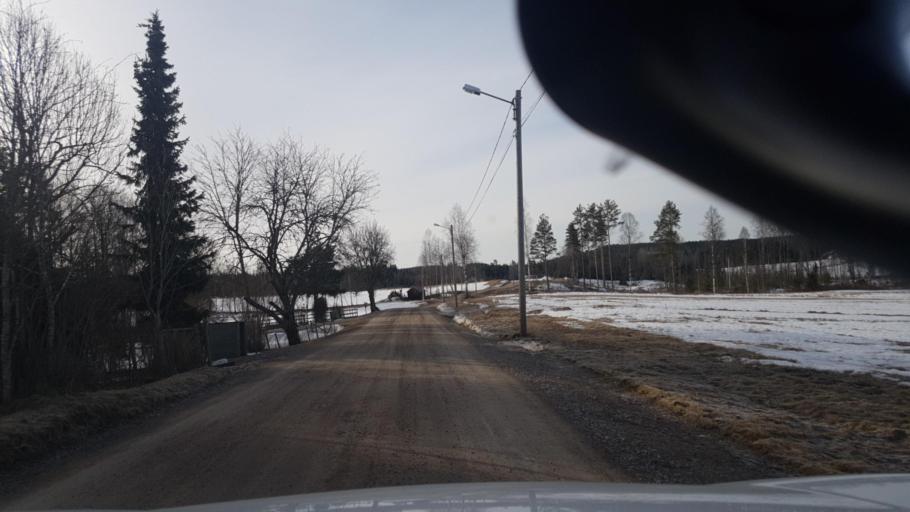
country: SE
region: Vaermland
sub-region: Arvika Kommun
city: Arvika
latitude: 59.8727
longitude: 12.6138
